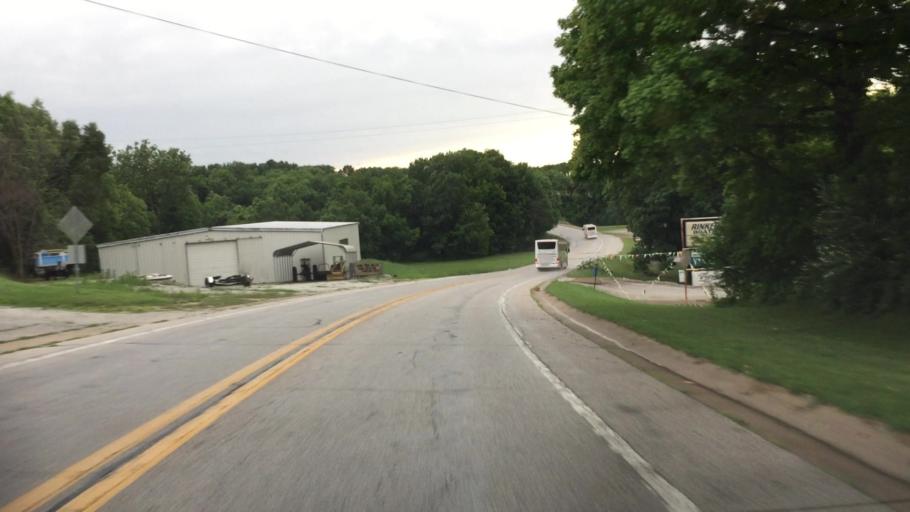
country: US
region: Illinois
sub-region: Hancock County
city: Hamilton
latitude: 40.4071
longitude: -91.3508
